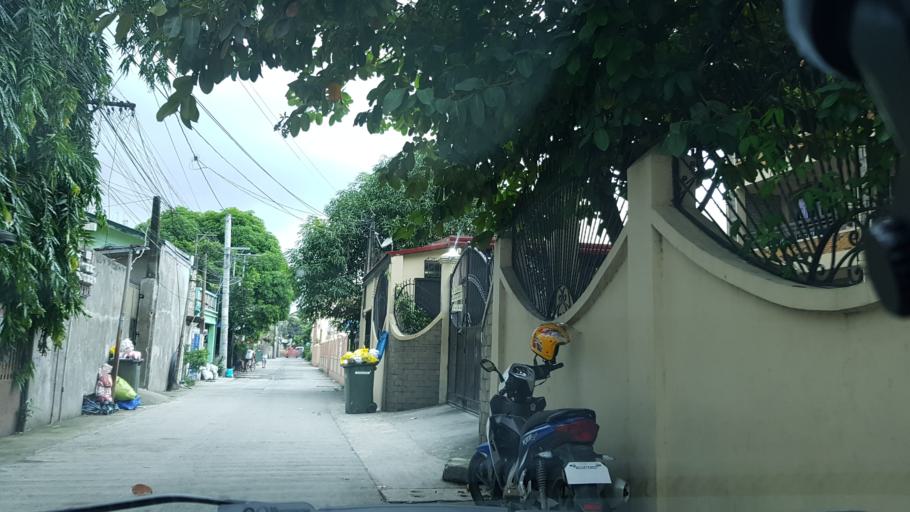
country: PH
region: Calabarzon
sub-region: Province of Rizal
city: Pateros
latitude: 14.5326
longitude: 121.0707
